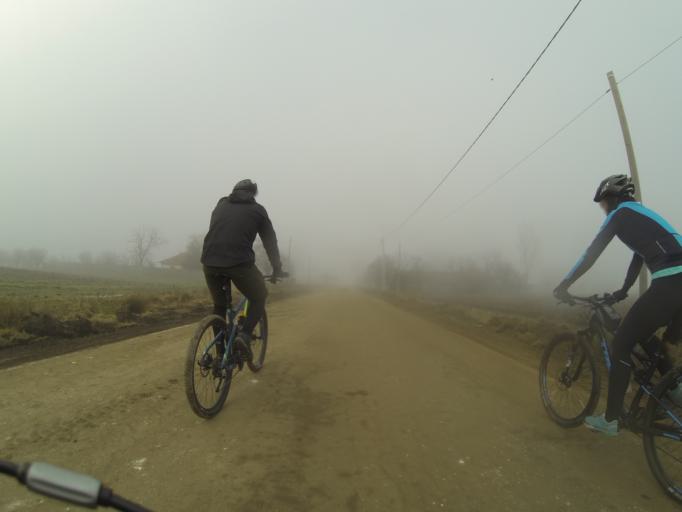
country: RO
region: Mehedinti
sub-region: Comuna Baclesu
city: Baclesu
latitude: 44.4820
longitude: 23.1053
